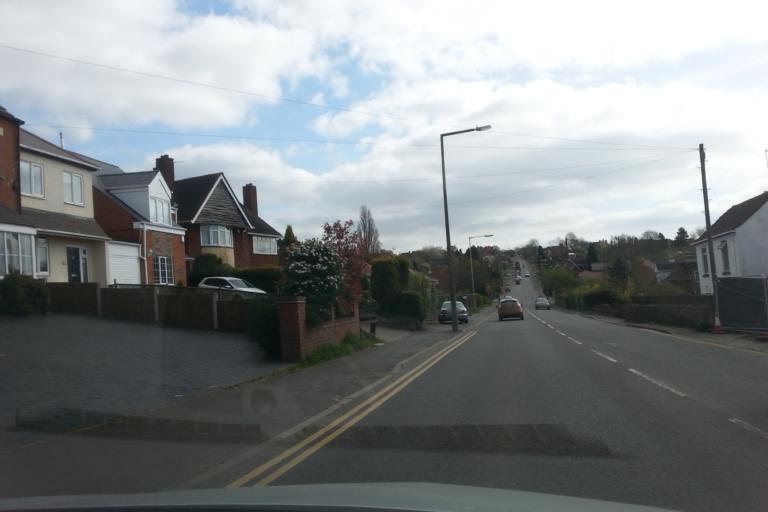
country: GB
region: England
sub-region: Dudley
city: Brierley Hill
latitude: 52.5146
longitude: -2.1316
